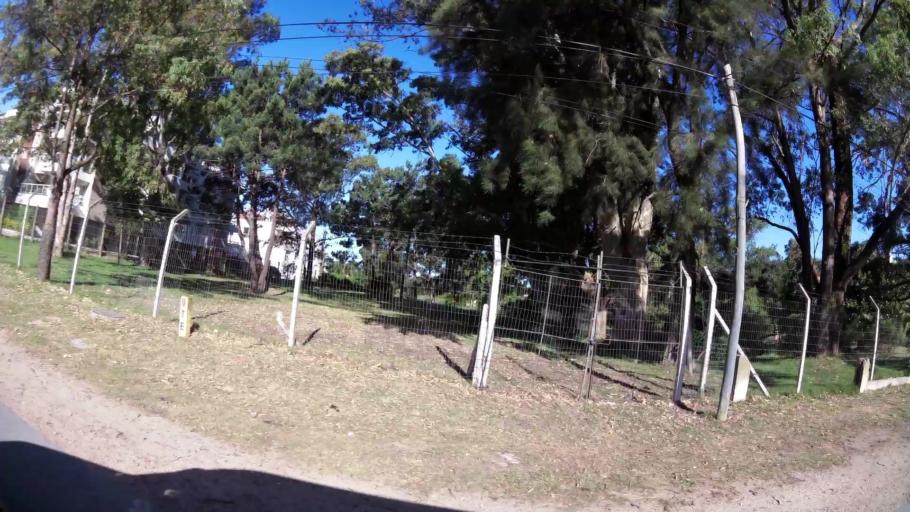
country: UY
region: Canelones
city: Barra de Carrasco
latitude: -34.8662
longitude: -56.0308
